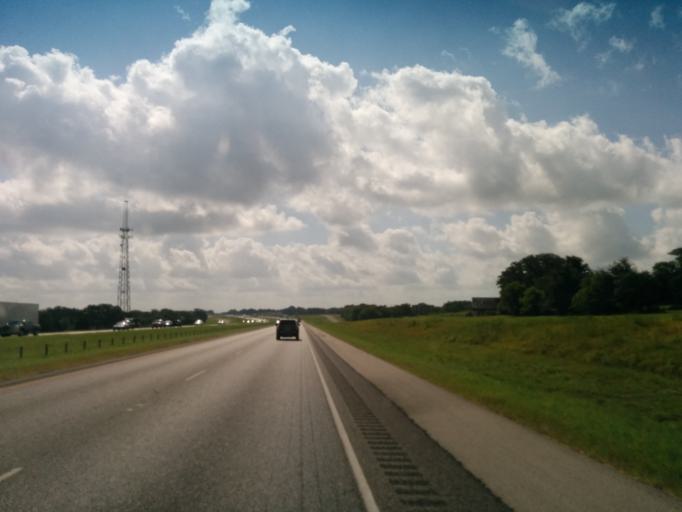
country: US
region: Texas
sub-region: Fayette County
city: Flatonia
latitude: 29.6927
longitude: -97.0150
